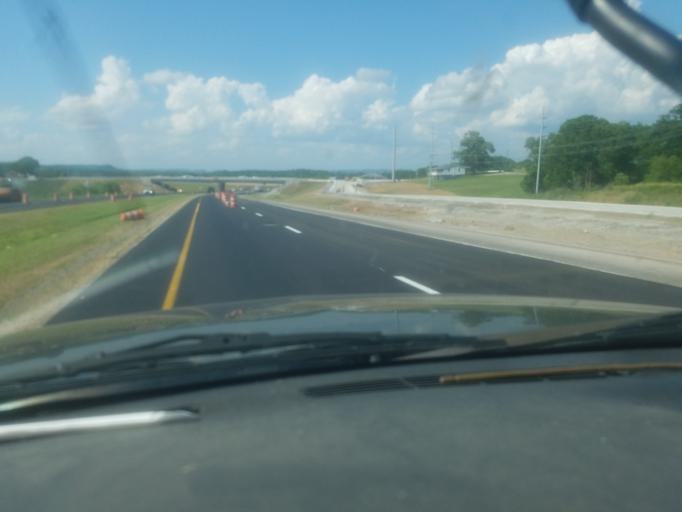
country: US
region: Tennessee
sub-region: Maury County
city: Mount Pleasant
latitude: 35.5409
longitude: -87.2211
